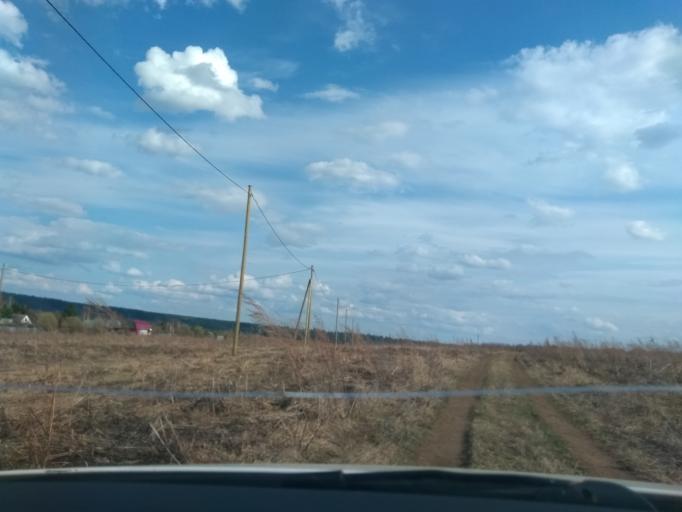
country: RU
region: Perm
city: Sylva
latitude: 57.8434
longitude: 56.7897
